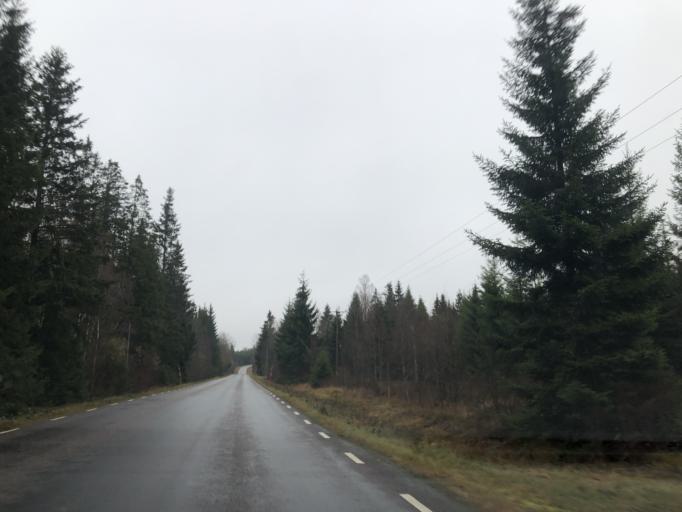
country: SE
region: Vaestra Goetaland
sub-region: Ulricehamns Kommun
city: Ulricehamn
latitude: 57.7476
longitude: 13.5279
